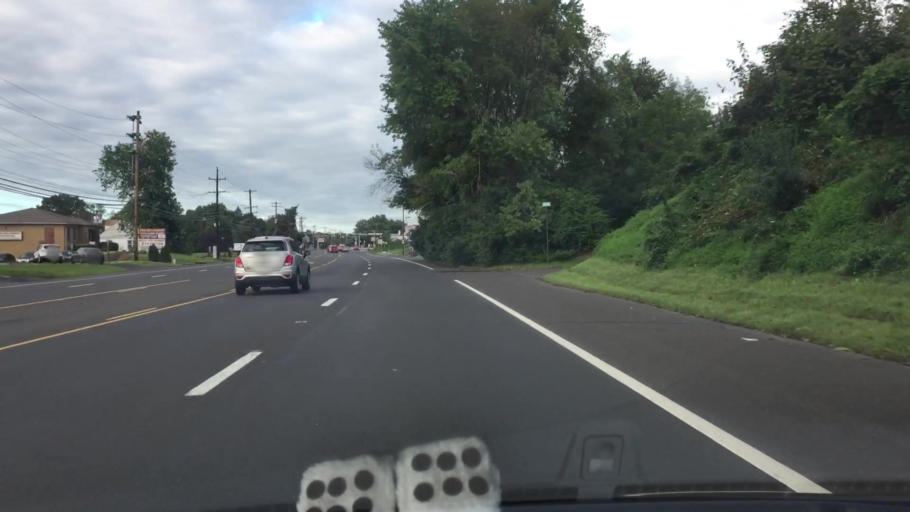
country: US
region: Pennsylvania
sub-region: Bucks County
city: Eddington
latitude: 40.1020
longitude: -74.9535
